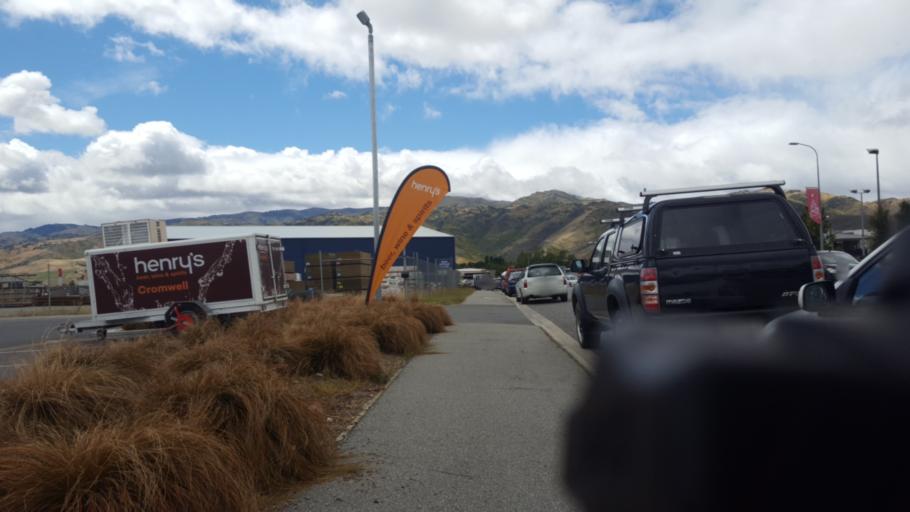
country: NZ
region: Otago
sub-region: Queenstown-Lakes District
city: Wanaka
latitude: -45.0353
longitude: 169.1951
